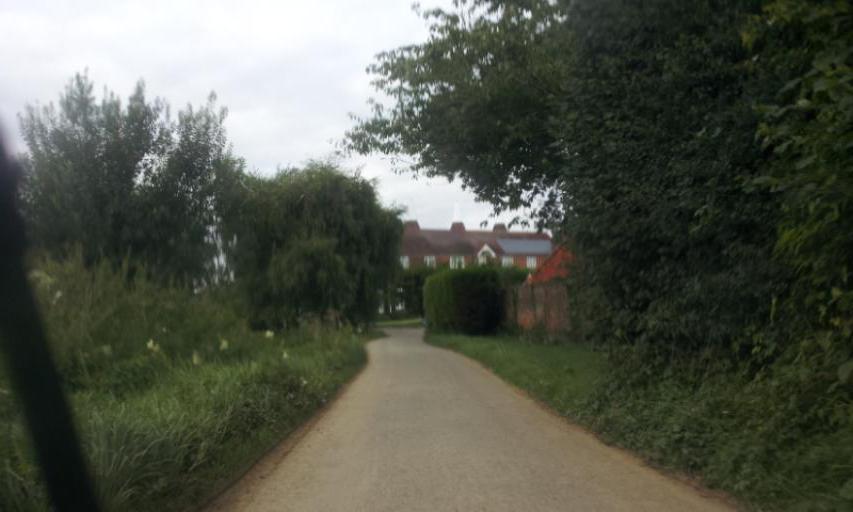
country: GB
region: England
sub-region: Kent
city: East Peckham
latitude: 51.2170
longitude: 0.3654
